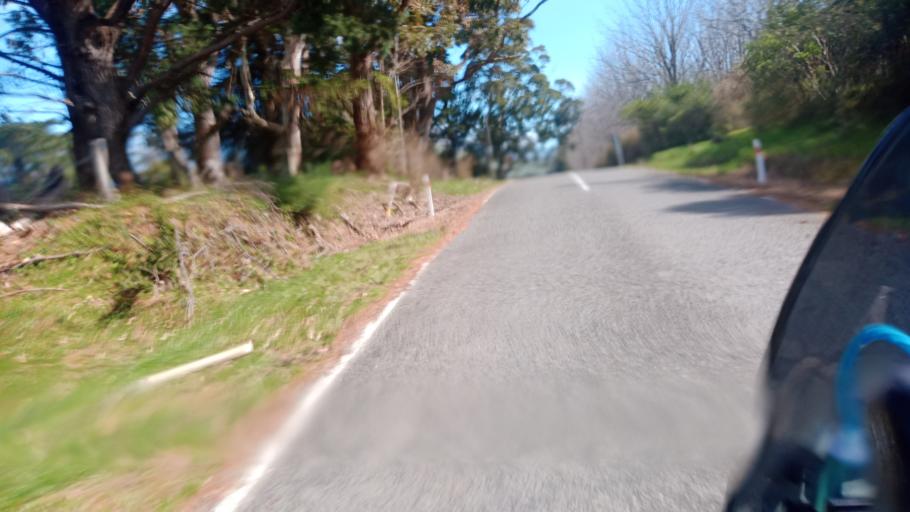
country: NZ
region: Gisborne
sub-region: Gisborne District
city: Gisborne
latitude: -37.8625
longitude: 178.2445
